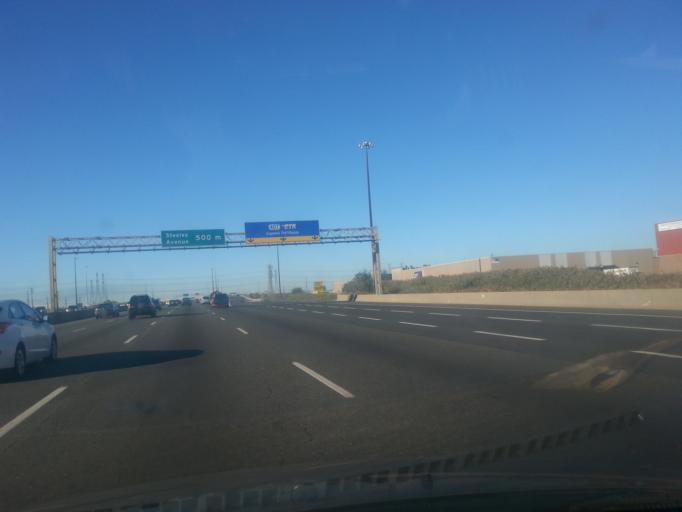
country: CA
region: Ontario
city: Concord
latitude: 43.7690
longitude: -79.5339
